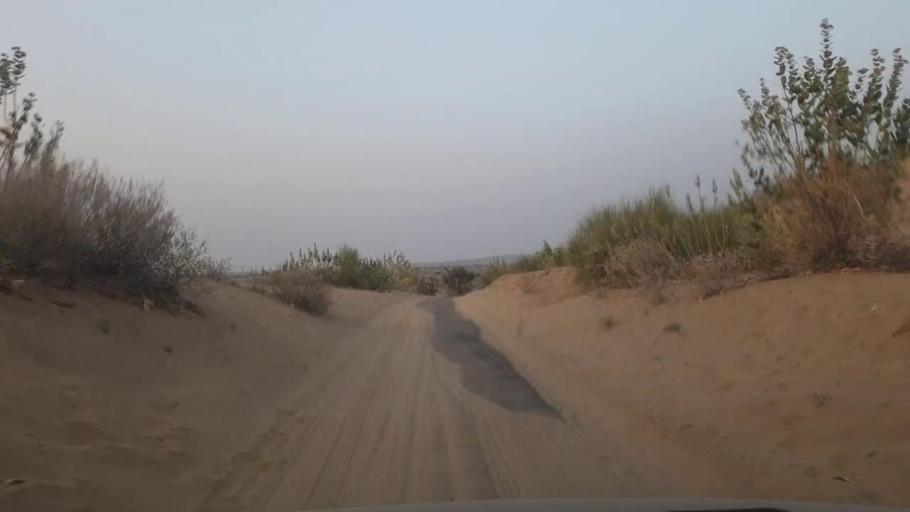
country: PK
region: Sindh
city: Umarkot
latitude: 25.2800
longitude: 70.0765
